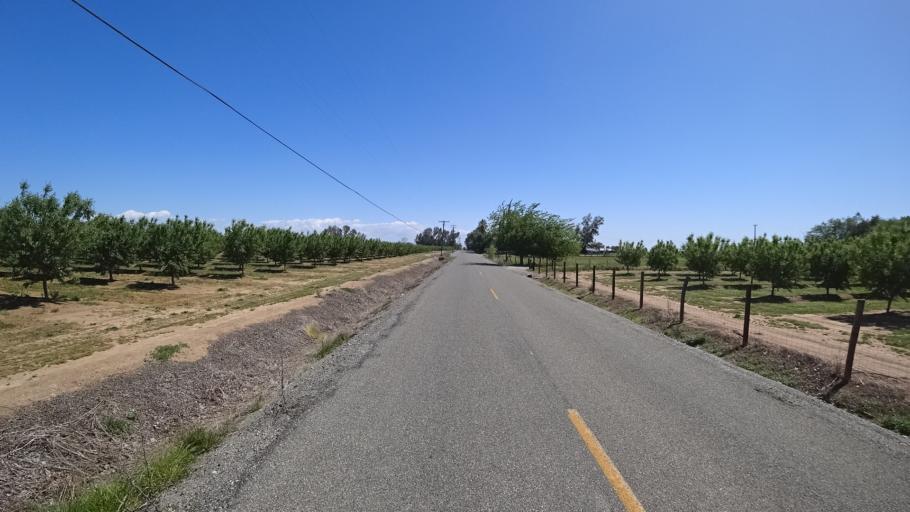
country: US
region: California
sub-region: Glenn County
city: Orland
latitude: 39.7873
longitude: -122.1910
